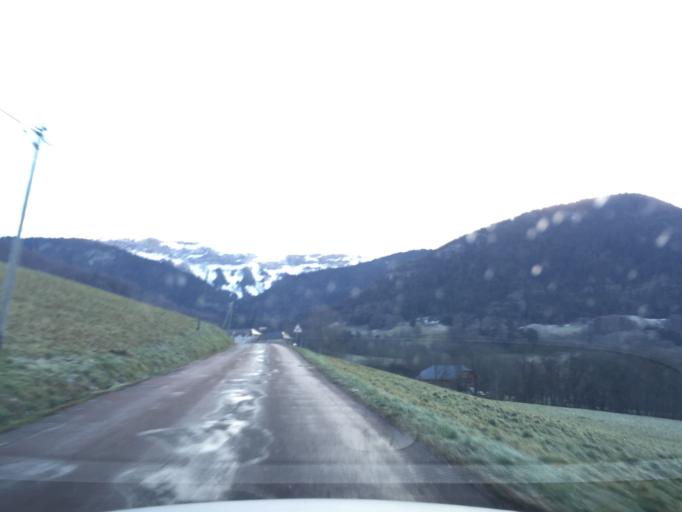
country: FR
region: Rhone-Alpes
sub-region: Departement de la Haute-Savoie
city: Doussard
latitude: 45.7378
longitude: 6.1345
